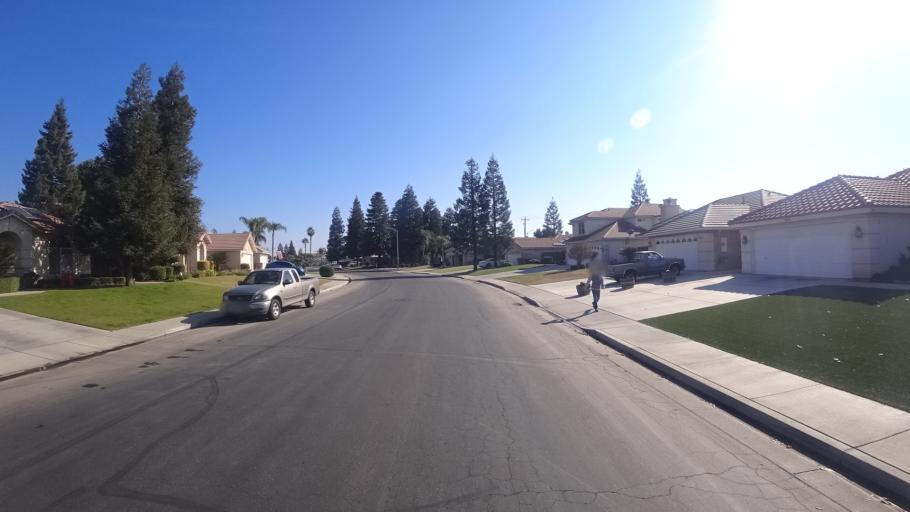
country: US
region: California
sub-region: Kern County
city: Greenacres
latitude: 35.3184
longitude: -119.1248
